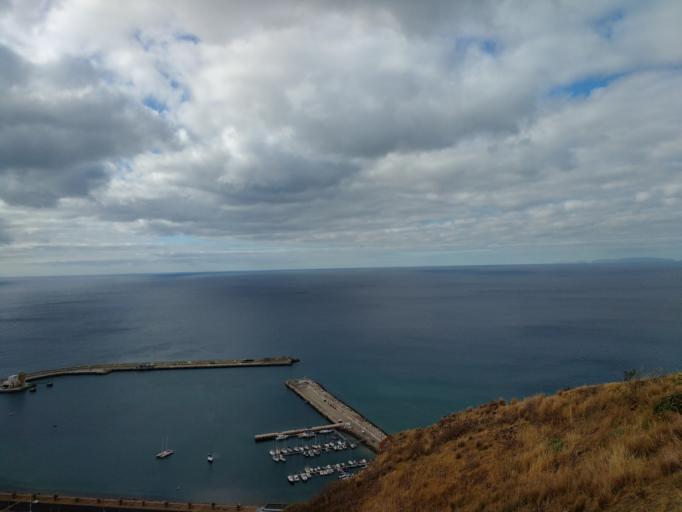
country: PT
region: Madeira
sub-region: Porto Santo
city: Vila de Porto Santo
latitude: 33.0663
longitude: -16.3173
